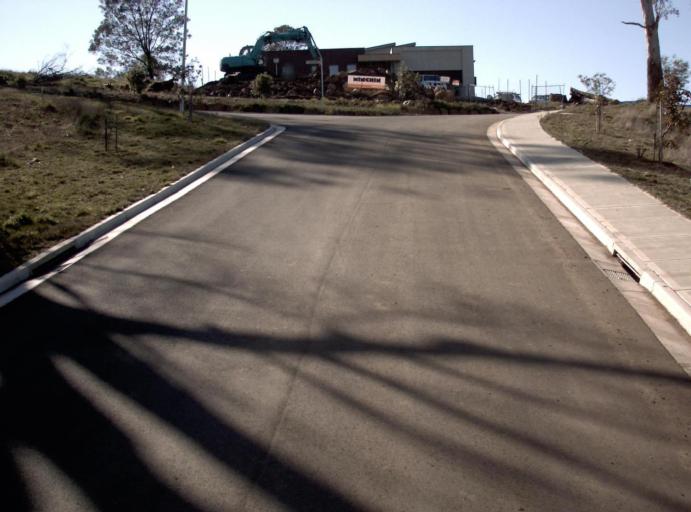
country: AU
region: Tasmania
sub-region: Launceston
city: Summerhill
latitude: -41.4737
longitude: 147.1502
